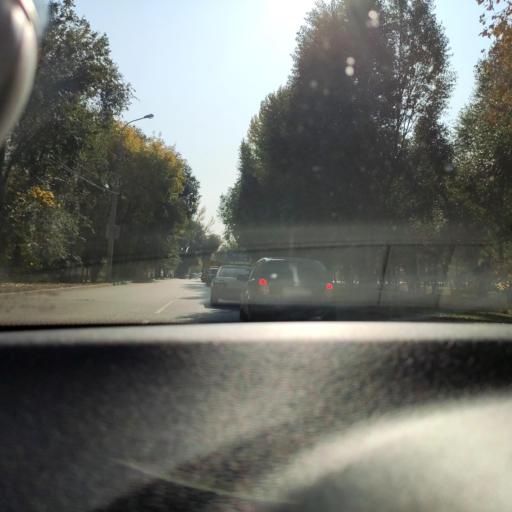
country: RU
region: Samara
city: Samara
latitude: 53.2034
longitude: 50.2211
